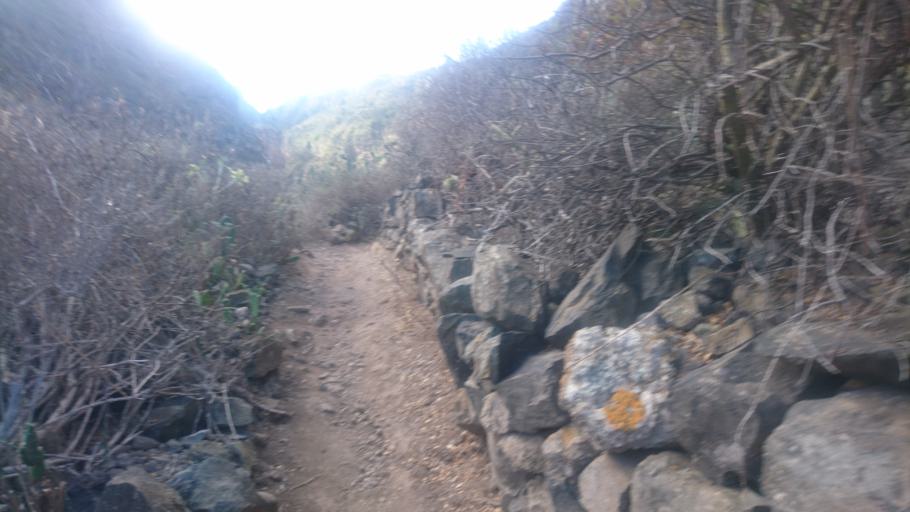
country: ES
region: Canary Islands
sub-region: Provincia de Santa Cruz de Tenerife
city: San Juan de la Rambla
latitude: 28.3896
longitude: -16.6267
